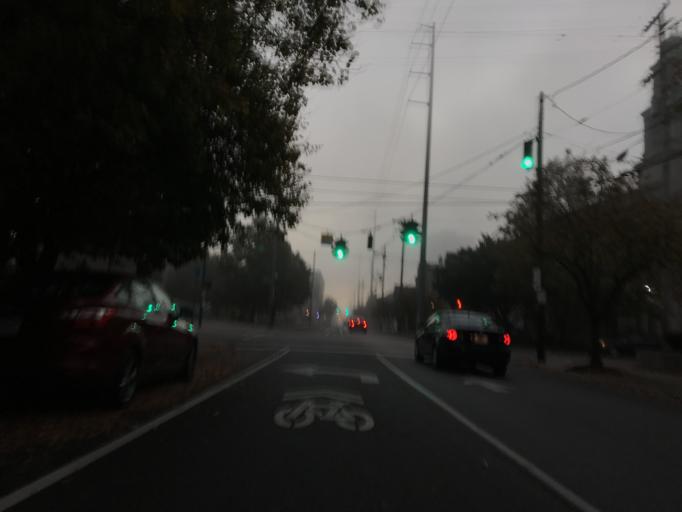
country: US
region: Kentucky
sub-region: Jefferson County
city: Louisville
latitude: 38.2390
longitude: -85.7601
